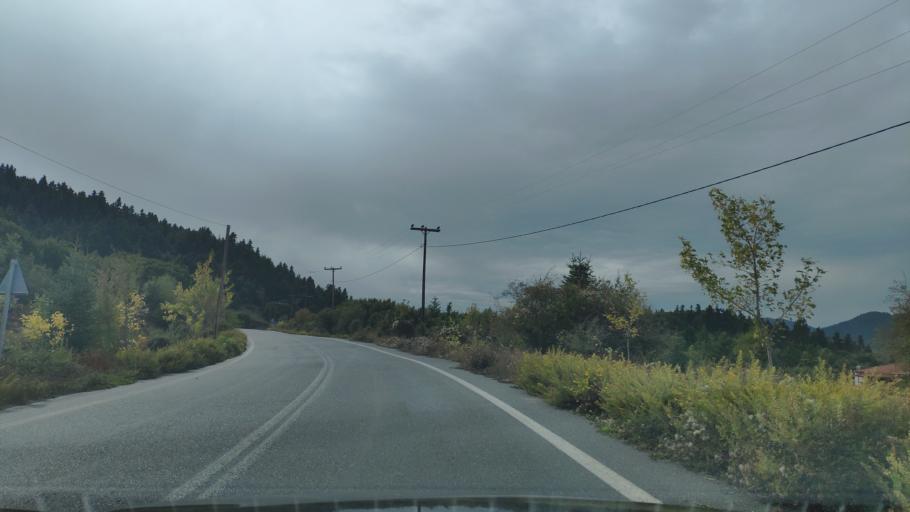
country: GR
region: Peloponnese
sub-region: Nomos Arkadias
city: Langadhia
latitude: 37.6653
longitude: 22.1926
